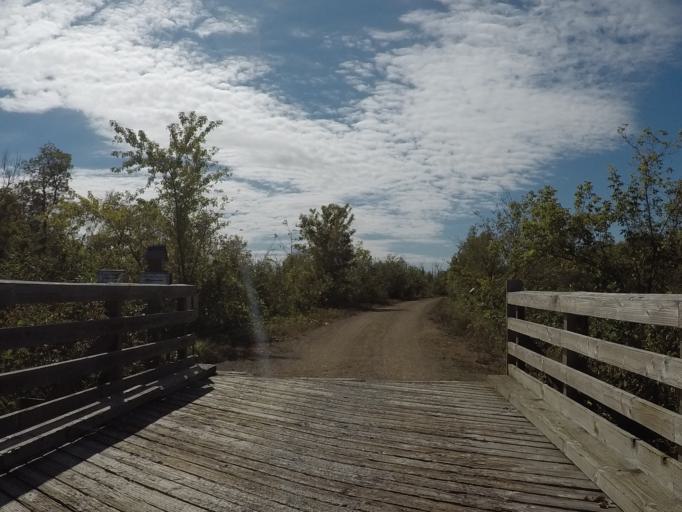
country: US
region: Wisconsin
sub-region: Richland County
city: Richland Center
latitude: 43.2622
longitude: -90.3019
